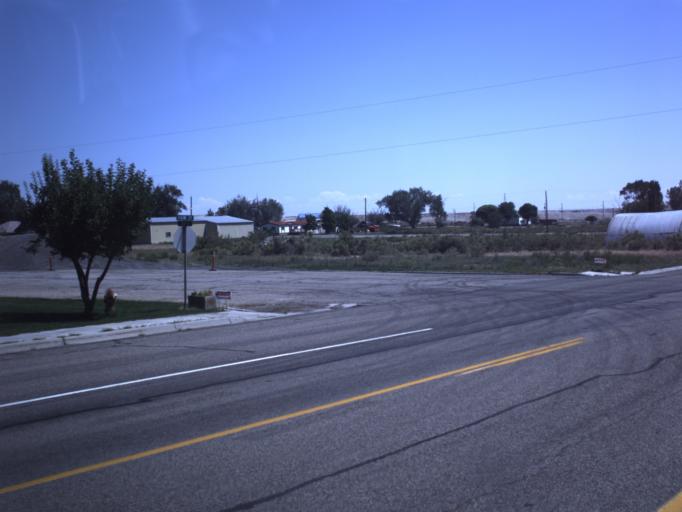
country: US
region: Utah
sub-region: Emery County
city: Ferron
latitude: 38.9231
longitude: -111.2471
